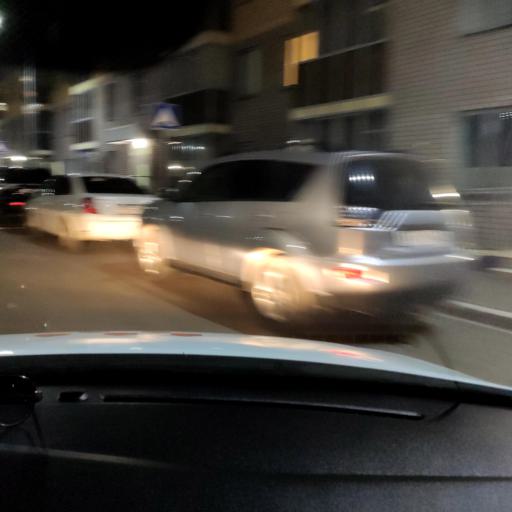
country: RU
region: Tatarstan
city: Staroye Arakchino
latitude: 55.8216
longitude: 49.0365
